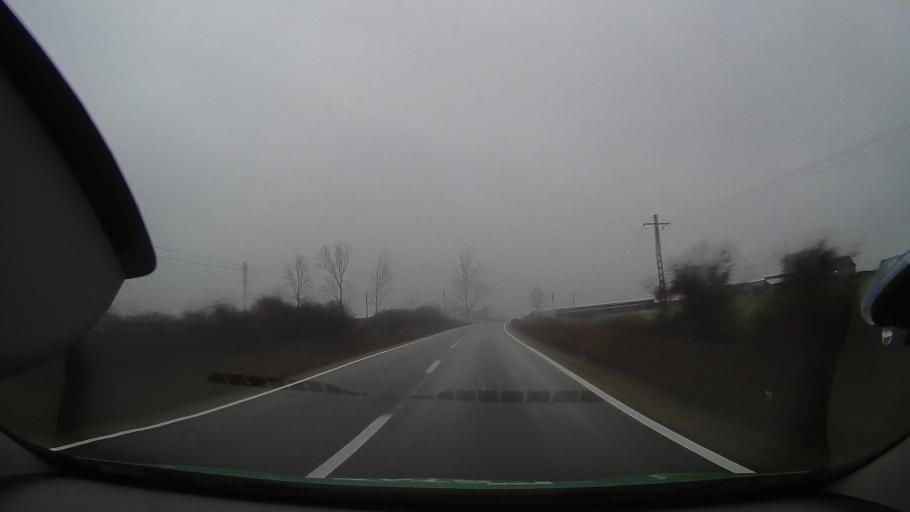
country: RO
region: Bihor
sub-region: Comuna Olcea
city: Calacea
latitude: 46.7174
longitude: 21.9533
